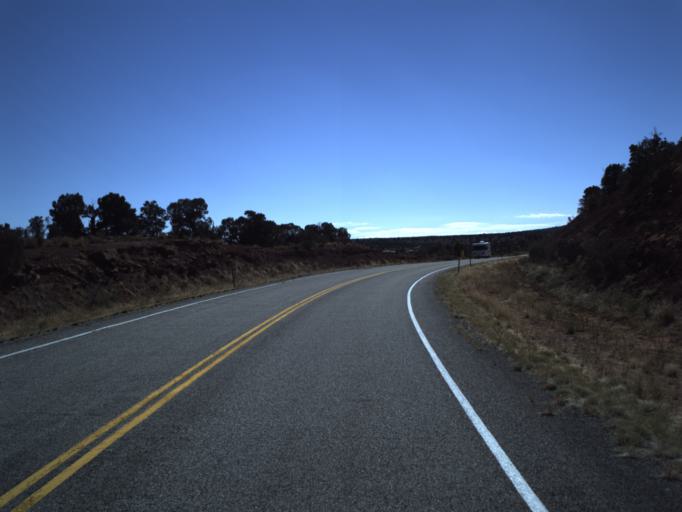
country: US
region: Utah
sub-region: San Juan County
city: Blanding
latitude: 37.5929
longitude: -110.0429
